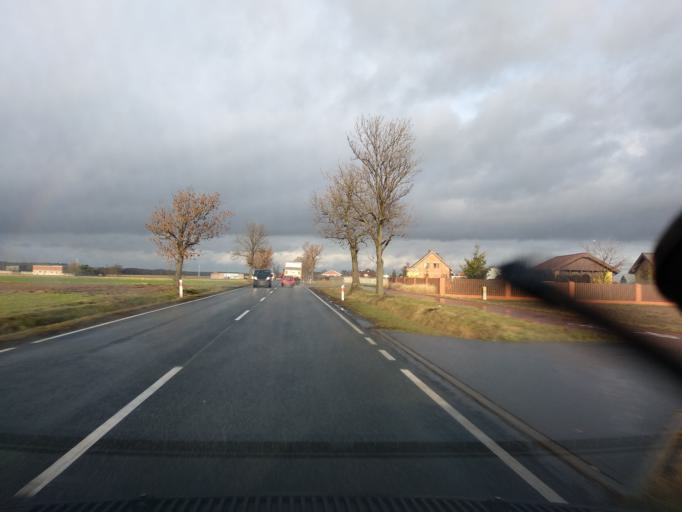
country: PL
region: Greater Poland Voivodeship
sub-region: Powiat koninski
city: Rychwal
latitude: 52.1115
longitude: 18.1676
